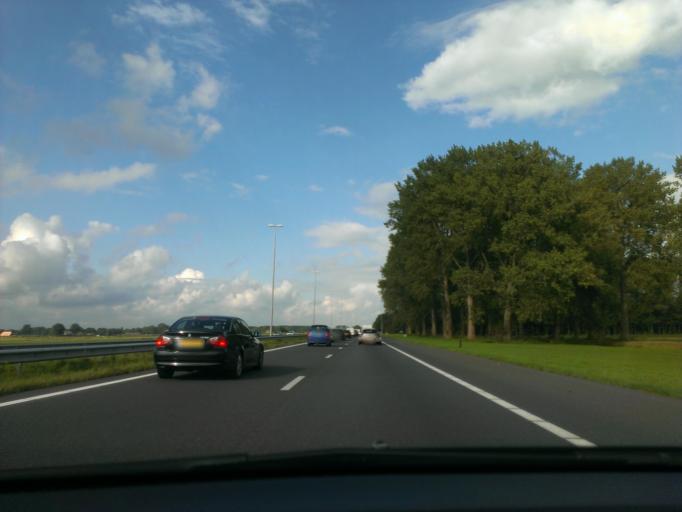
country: NL
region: Gelderland
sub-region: Gemeente Epe
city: Vaassen
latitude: 52.2725
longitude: 6.0043
